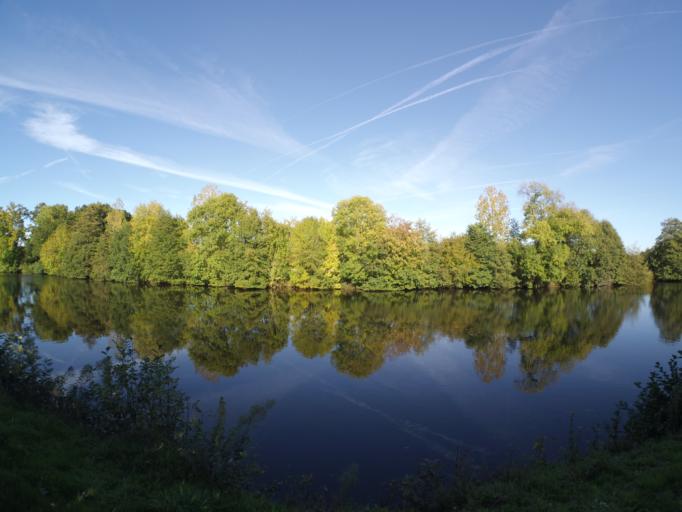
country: FR
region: Brittany
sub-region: Departement du Morbihan
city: Peillac
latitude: 47.7345
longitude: -2.2250
